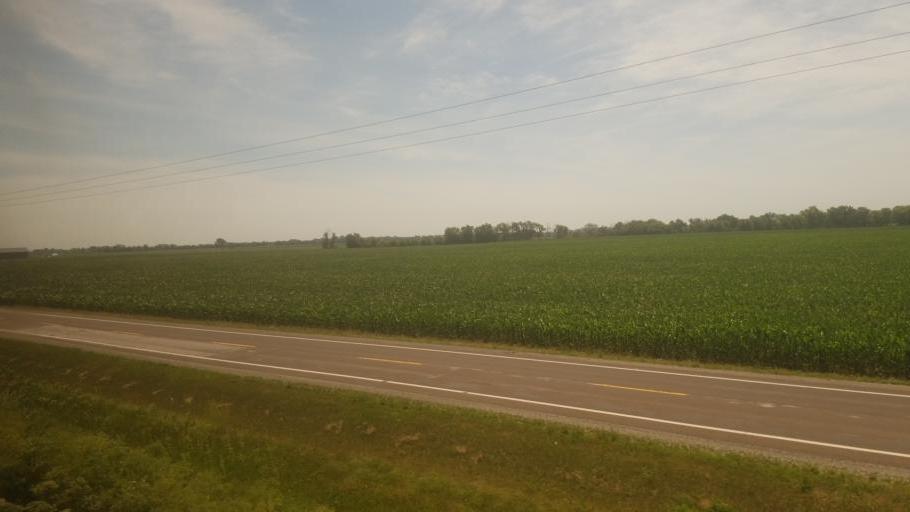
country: US
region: Missouri
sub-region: Carroll County
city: Carrollton
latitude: 39.3158
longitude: -93.6195
